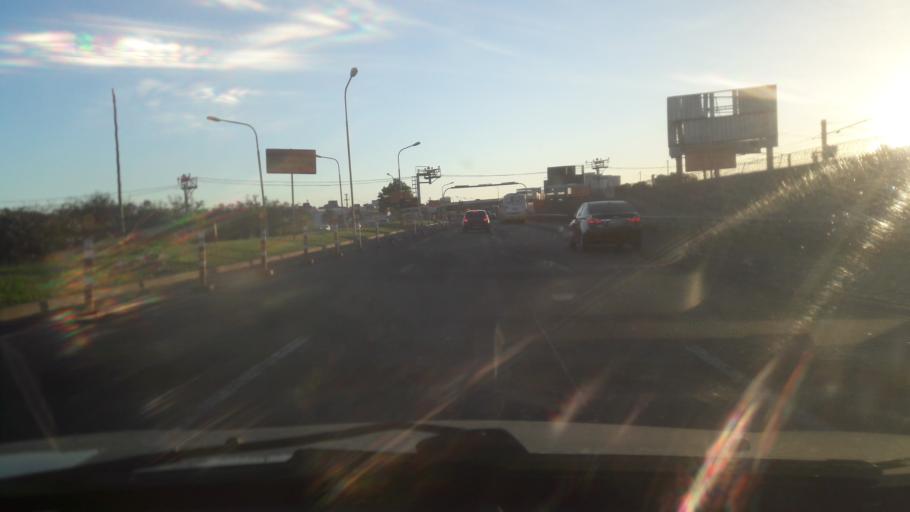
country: BR
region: Rio Grande do Sul
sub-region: Porto Alegre
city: Porto Alegre
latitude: -29.9936
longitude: -51.1872
